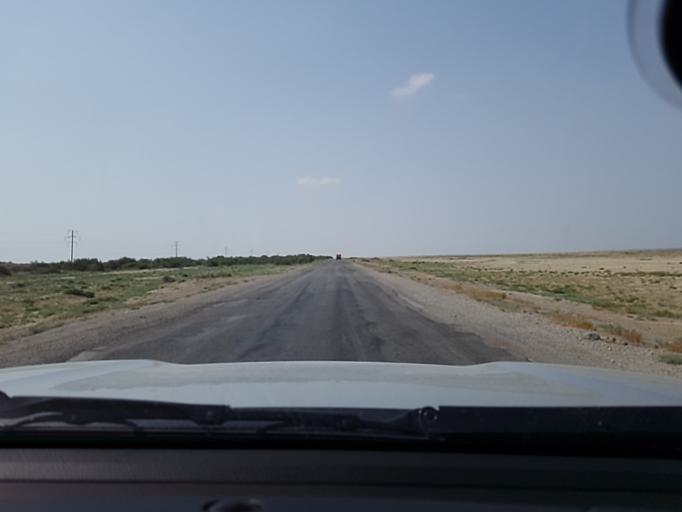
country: TM
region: Balkan
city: Gumdag
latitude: 38.9297
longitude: 54.5905
